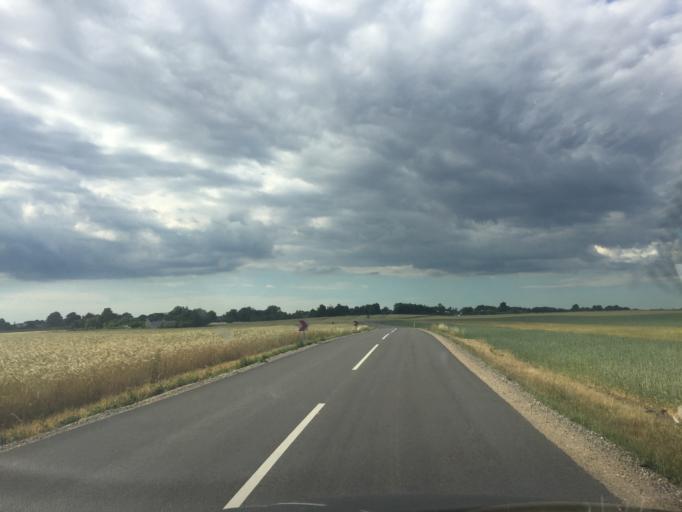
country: DK
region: Capital Region
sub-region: Egedal Kommune
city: Vekso
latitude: 55.7073
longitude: 12.2216
